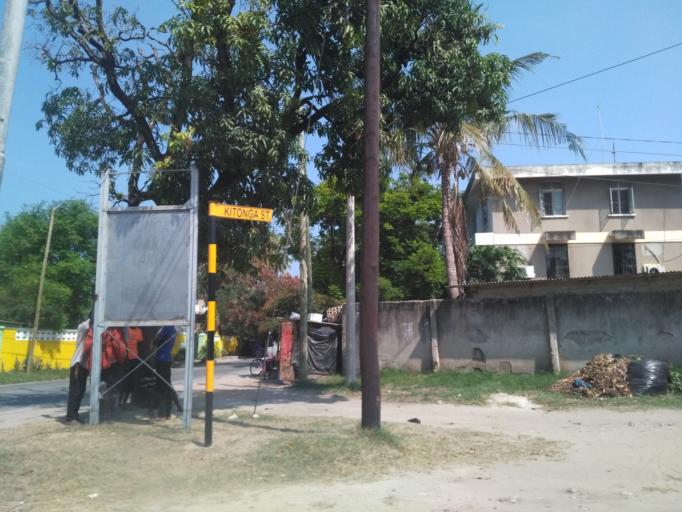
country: TZ
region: Dar es Salaam
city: Dar es Salaam
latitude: -6.8015
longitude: 39.2829
